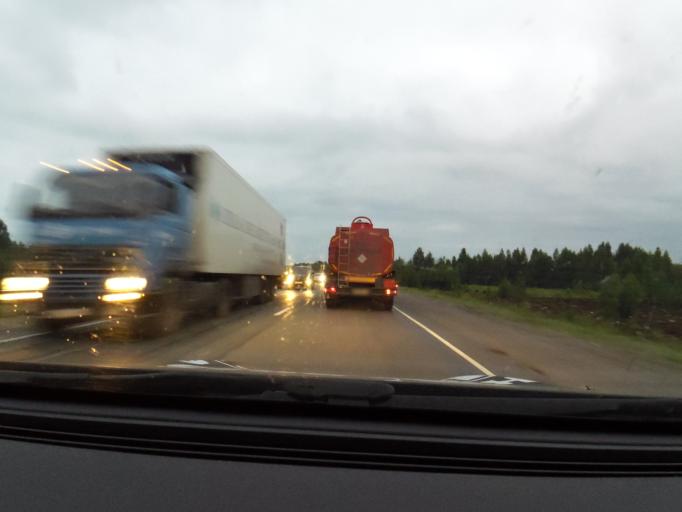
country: RU
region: Perm
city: Krasnokamsk
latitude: 58.0890
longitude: 55.7205
